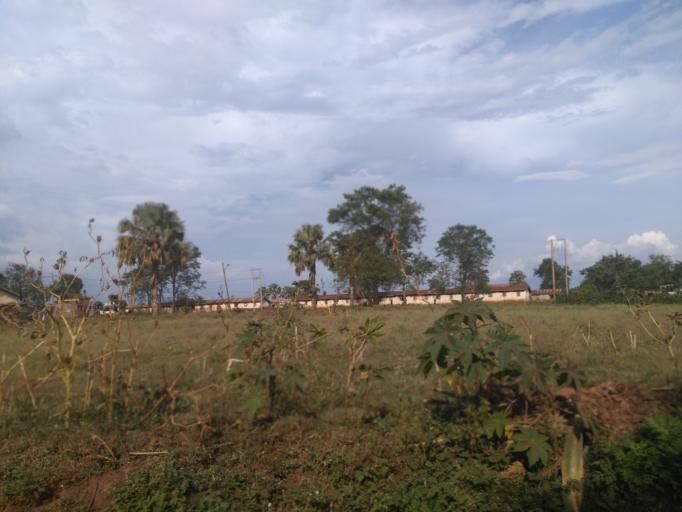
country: UG
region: Eastern Region
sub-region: Jinja District
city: Jinja
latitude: 0.4158
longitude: 33.2148
